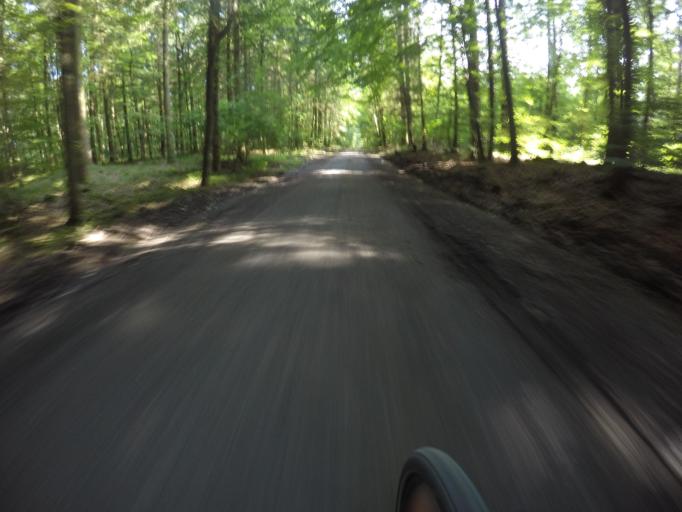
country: DE
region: Baden-Wuerttemberg
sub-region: Regierungsbezirk Stuttgart
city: Weissach
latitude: 48.8701
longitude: 8.9026
